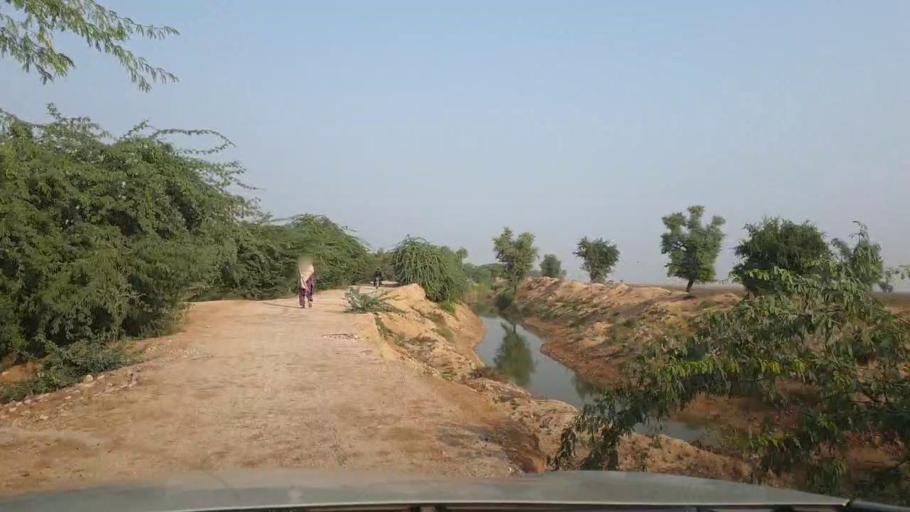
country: PK
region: Sindh
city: Sehwan
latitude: 26.3457
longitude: 67.7237
